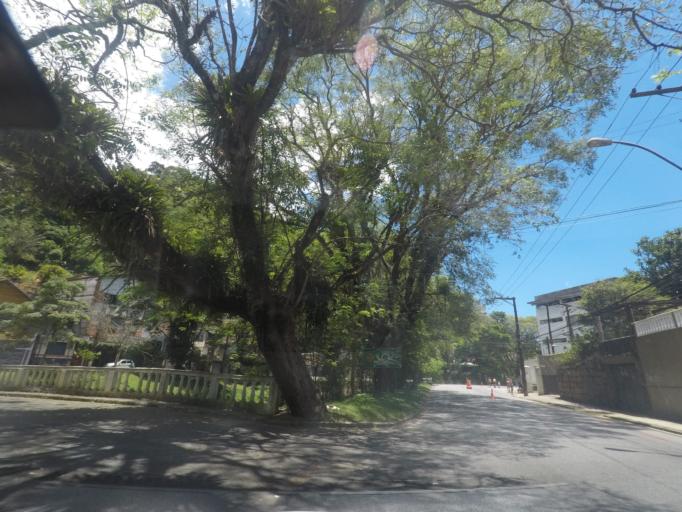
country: BR
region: Rio de Janeiro
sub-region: Petropolis
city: Petropolis
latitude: -22.4937
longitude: -43.1795
